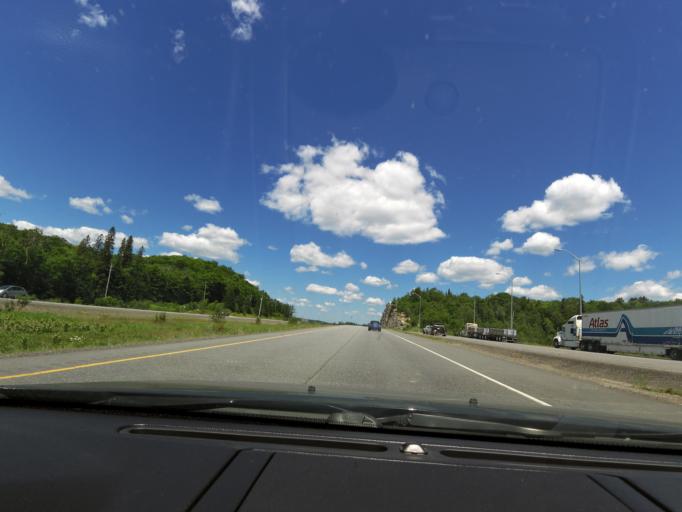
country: CA
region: Ontario
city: Huntsville
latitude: 45.4213
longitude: -79.2373
